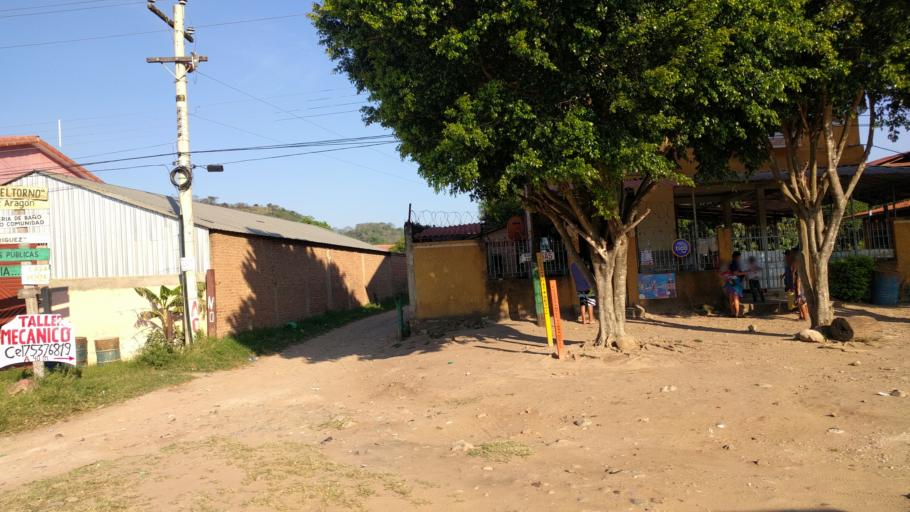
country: BO
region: Santa Cruz
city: Jorochito
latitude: -18.0978
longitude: -63.4516
